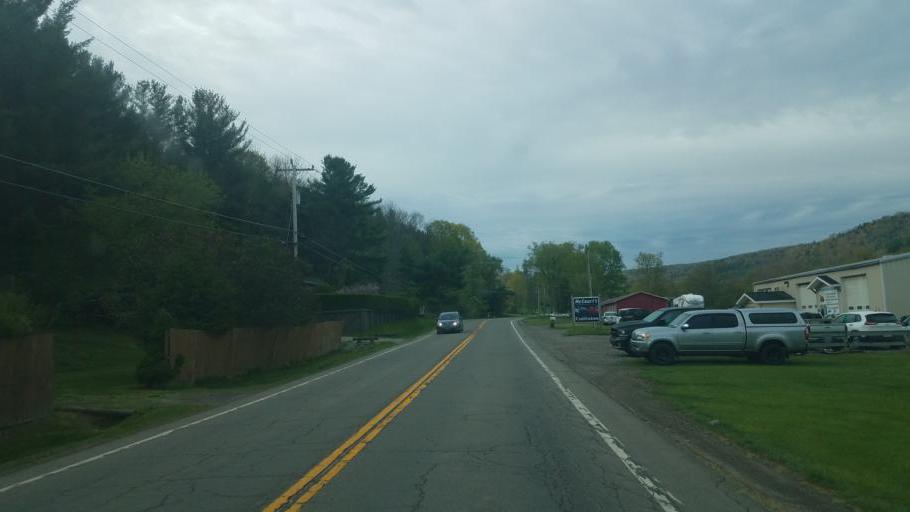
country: US
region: New York
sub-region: Steuben County
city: Canisteo
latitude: 42.2286
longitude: -77.5751
